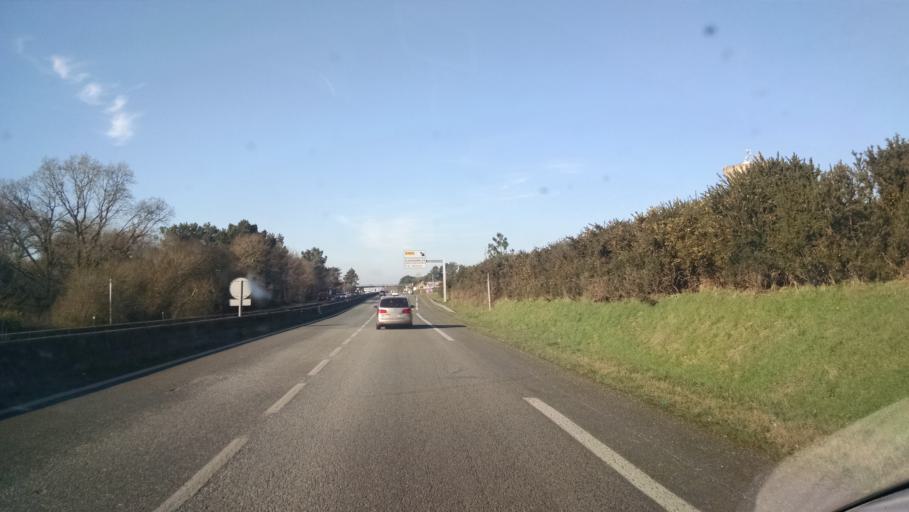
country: FR
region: Brittany
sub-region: Departement du Morbihan
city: Plougoumelen
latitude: 47.6640
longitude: -2.8922
